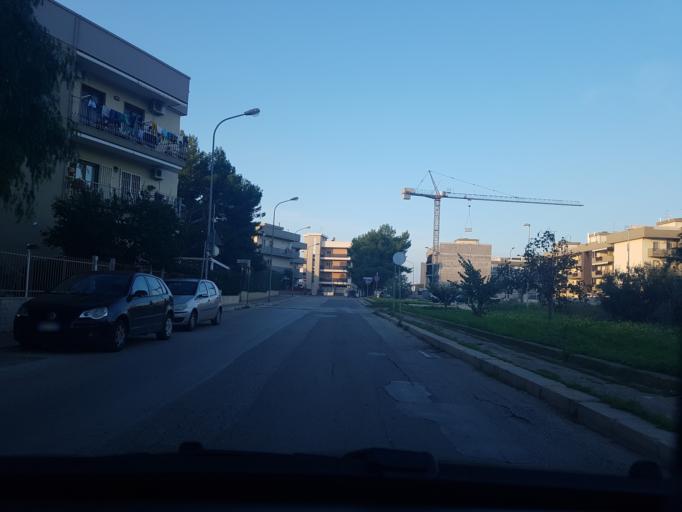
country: IT
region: Apulia
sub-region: Provincia di Bari
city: Bitritto
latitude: 41.0433
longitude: 16.8305
